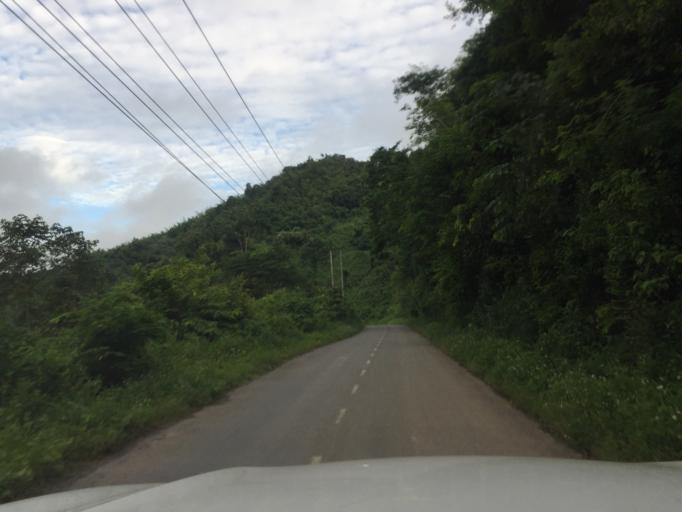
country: LA
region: Phongsali
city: Khoa
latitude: 21.1014
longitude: 102.2800
